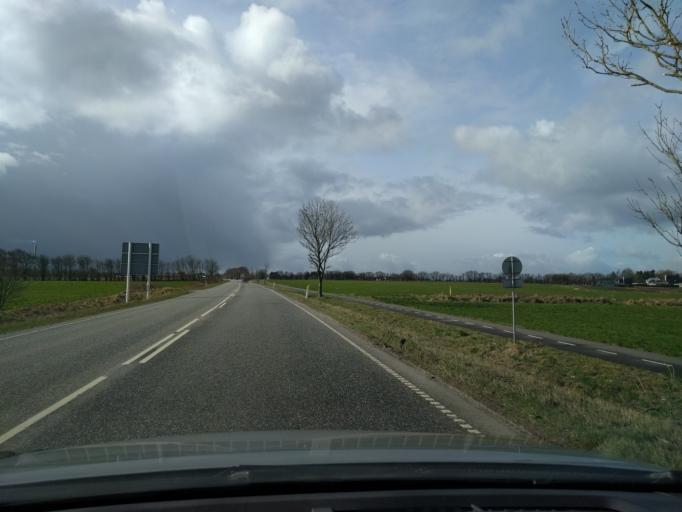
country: DK
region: South Denmark
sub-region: Kolding Kommune
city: Vamdrup
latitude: 55.4389
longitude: 9.3286
